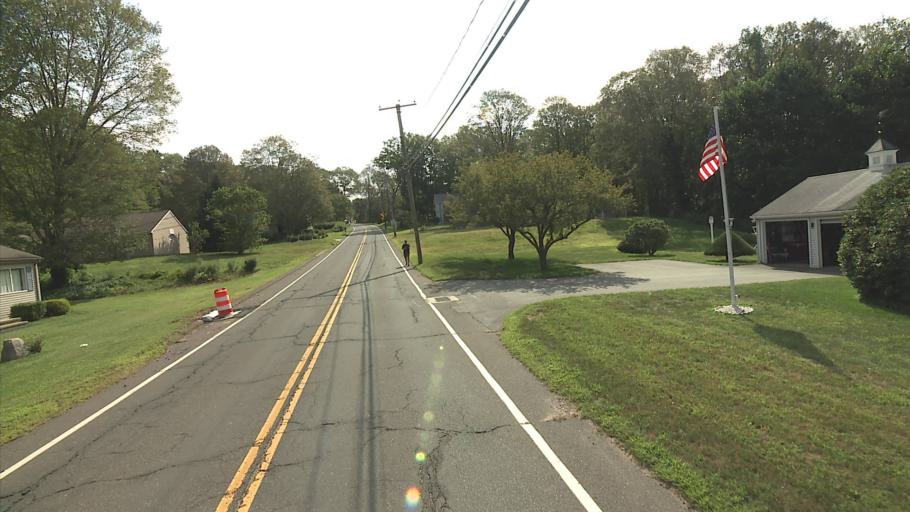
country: US
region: Connecticut
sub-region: Middlesex County
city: Moodus
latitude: 41.5130
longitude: -72.4316
